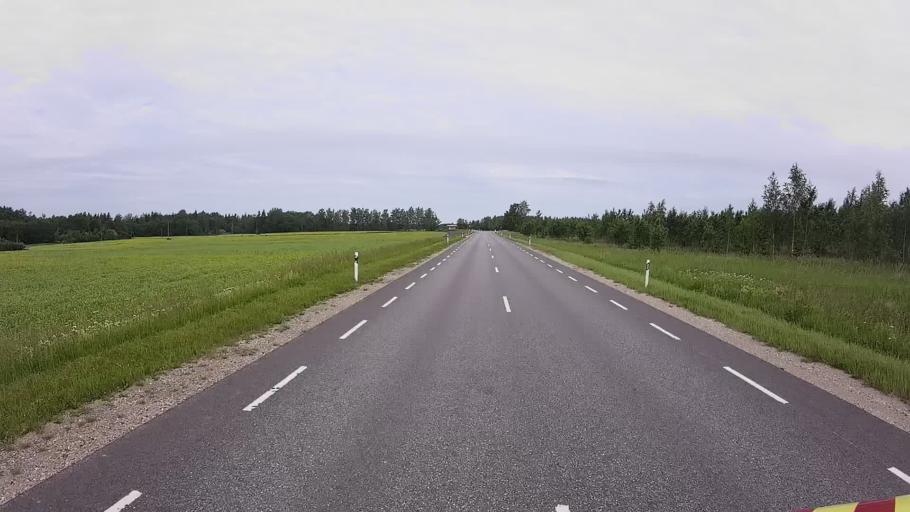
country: EE
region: Viljandimaa
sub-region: Karksi vald
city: Karksi-Nuia
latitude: 58.1544
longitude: 25.5957
